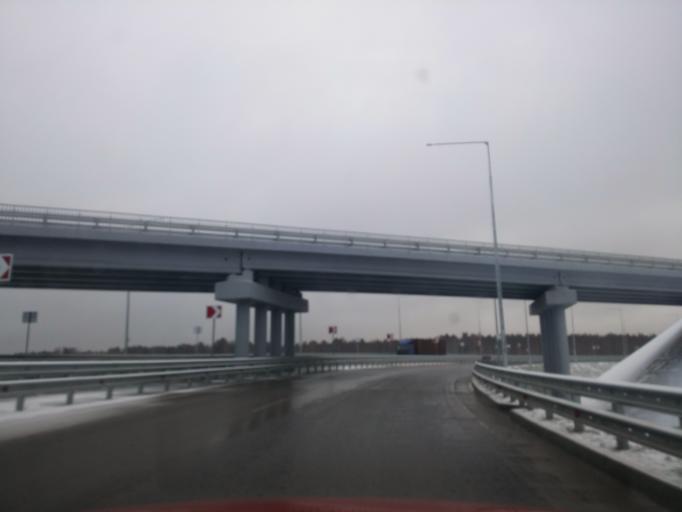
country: RU
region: Tverskaya
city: Likhoslavl'
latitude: 56.9515
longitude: 35.5141
